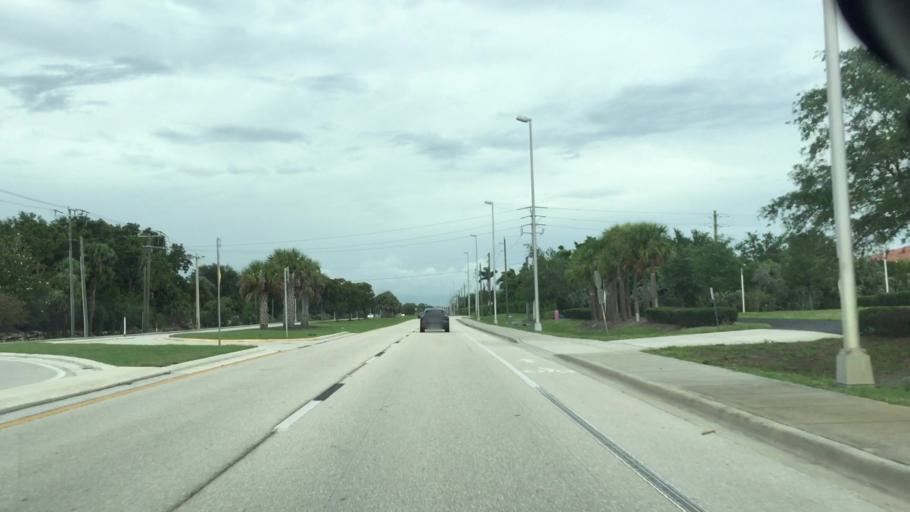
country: US
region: Florida
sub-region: Lee County
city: Estero
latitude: 26.4407
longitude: -81.7885
